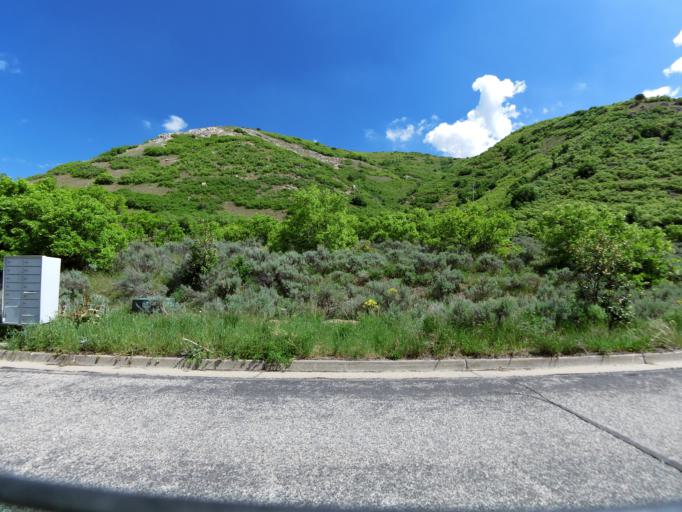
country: US
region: Utah
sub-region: Weber County
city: Uintah
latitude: 41.1658
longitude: -111.9218
